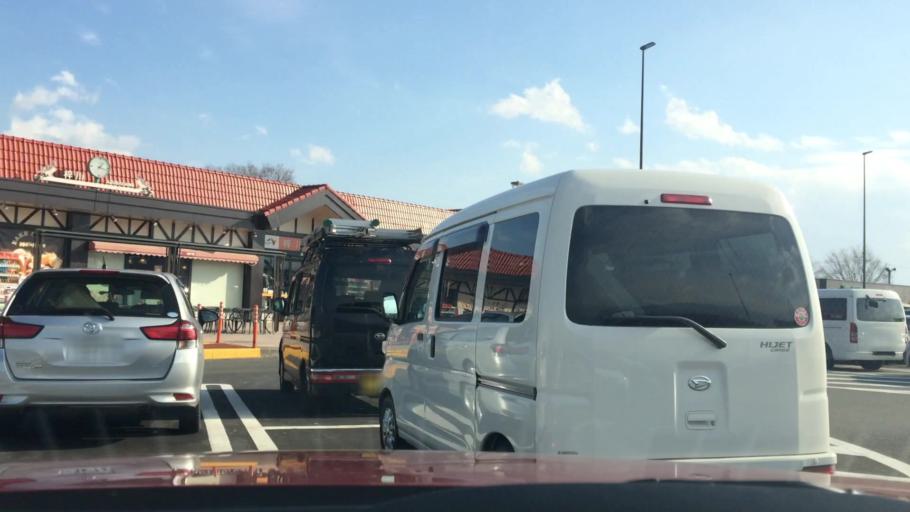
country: JP
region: Nagano
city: Toyoshina
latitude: 36.2711
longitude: 137.9316
